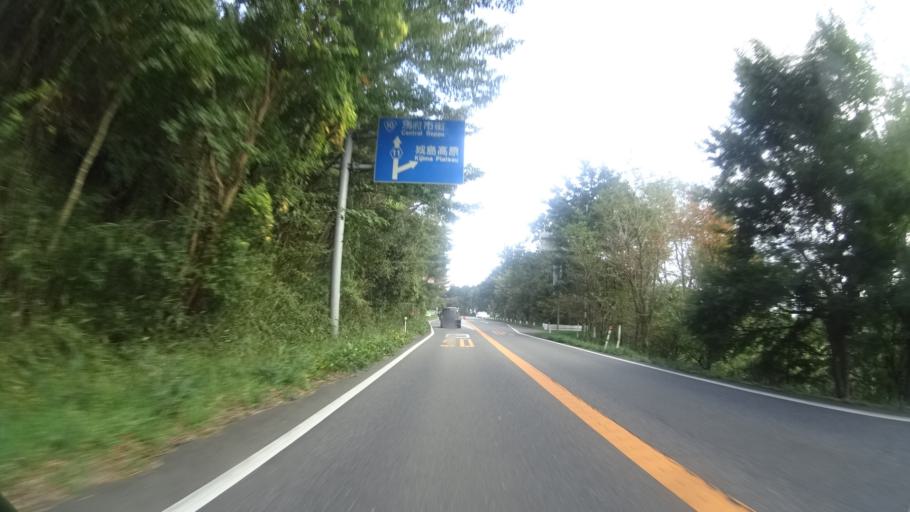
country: JP
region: Oita
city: Beppu
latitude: 33.2693
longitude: 131.4247
